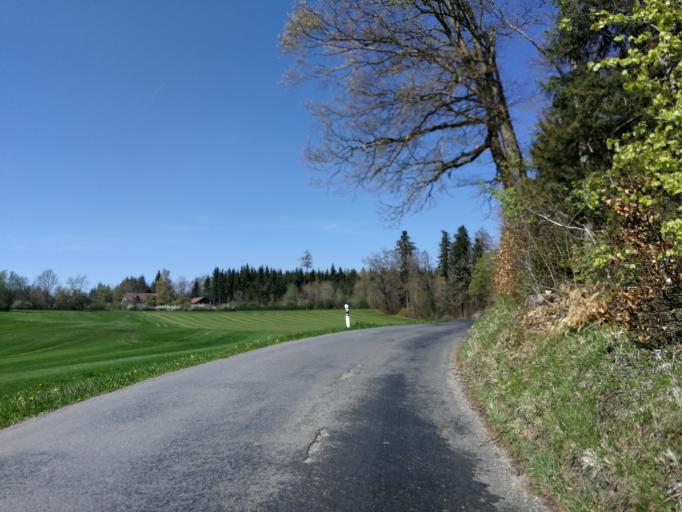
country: CH
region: Zurich
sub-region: Bezirk Uster
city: Aesch
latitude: 47.3113
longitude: 8.6597
